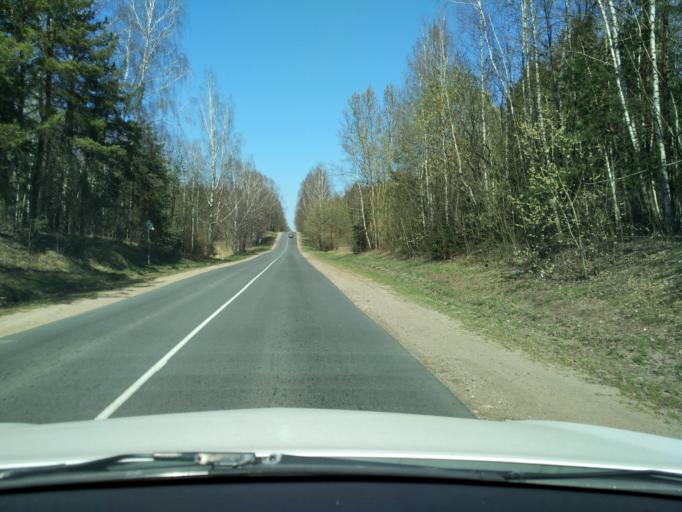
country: BY
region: Minsk
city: Slabada
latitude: 53.9727
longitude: 27.9515
